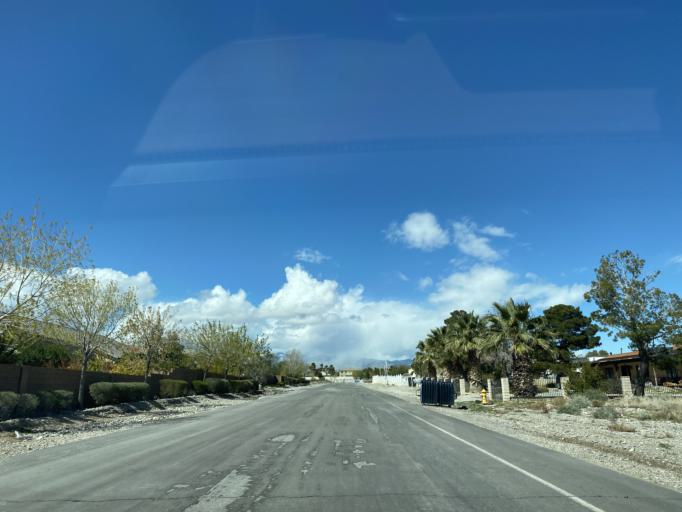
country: US
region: Nevada
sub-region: Clark County
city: North Las Vegas
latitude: 36.3195
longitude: -115.2833
